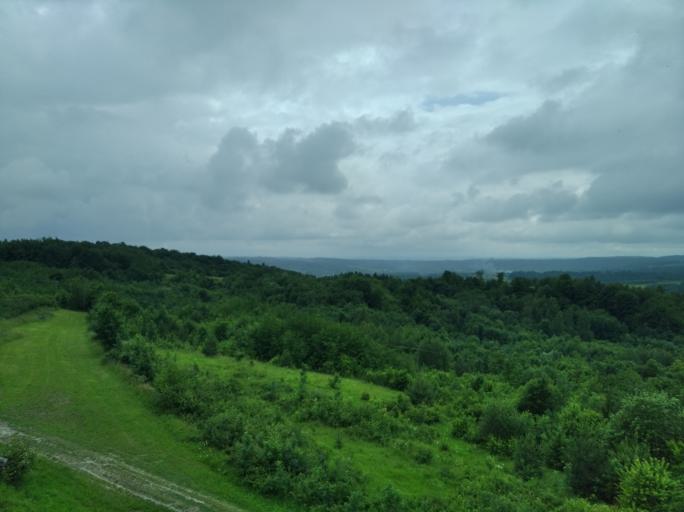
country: PL
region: Subcarpathian Voivodeship
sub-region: Powiat jaroslawski
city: Pruchnik
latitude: 49.8888
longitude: 22.5121
